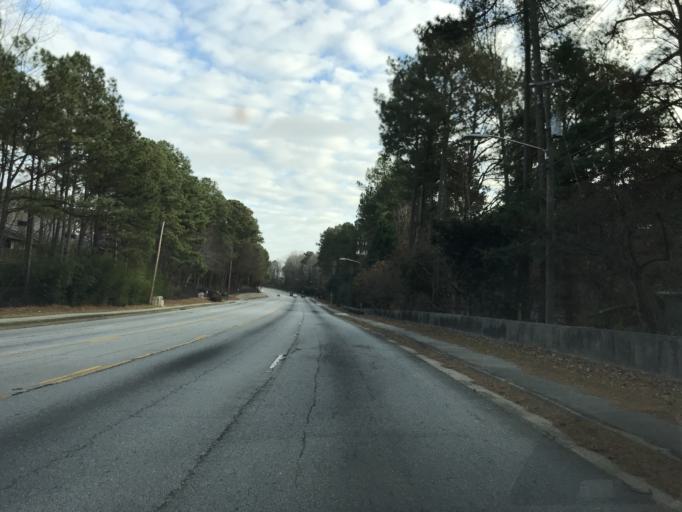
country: US
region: Georgia
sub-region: DeKalb County
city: Tucker
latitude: 33.8882
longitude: -84.2264
